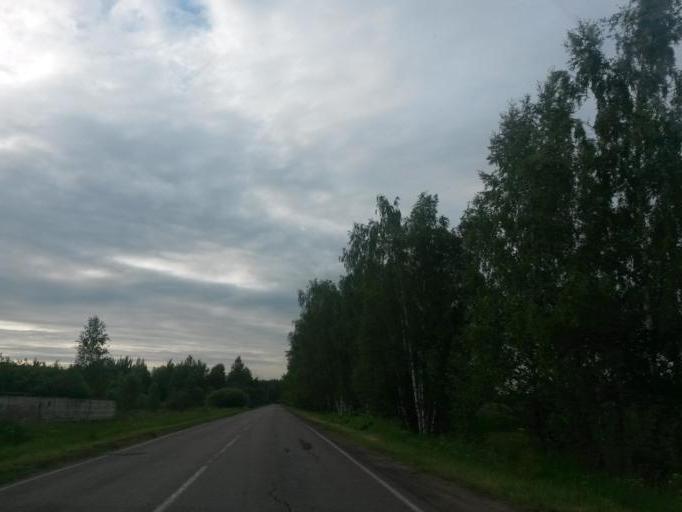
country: RU
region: Moskovskaya
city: Melikhovo
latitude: 55.2091
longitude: 37.6914
